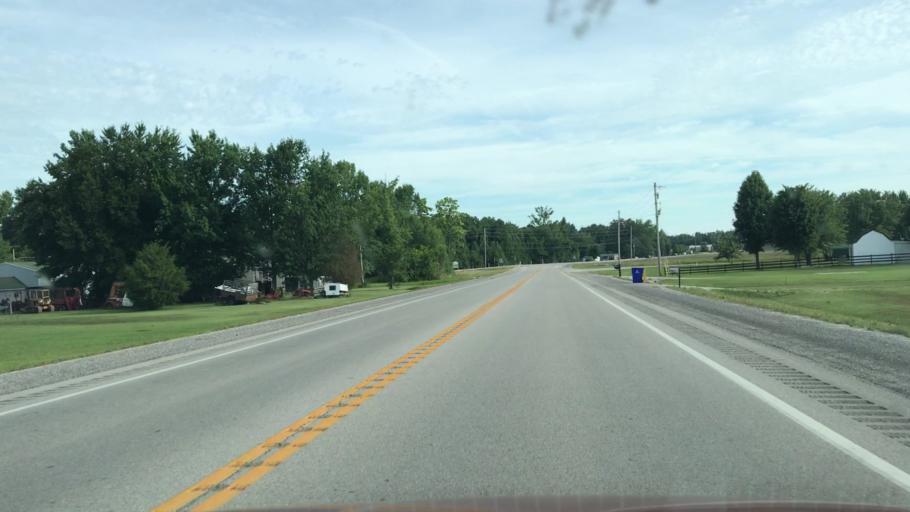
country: US
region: Kentucky
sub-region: Edmonson County
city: Brownsville
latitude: 37.1250
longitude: -86.2348
